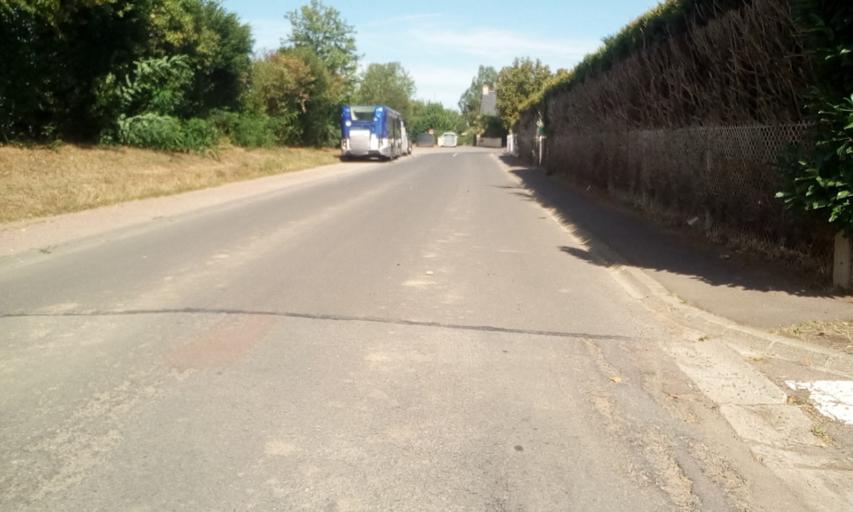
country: FR
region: Lower Normandy
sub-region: Departement du Calvados
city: Eterville
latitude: 49.1444
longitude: -0.4316
